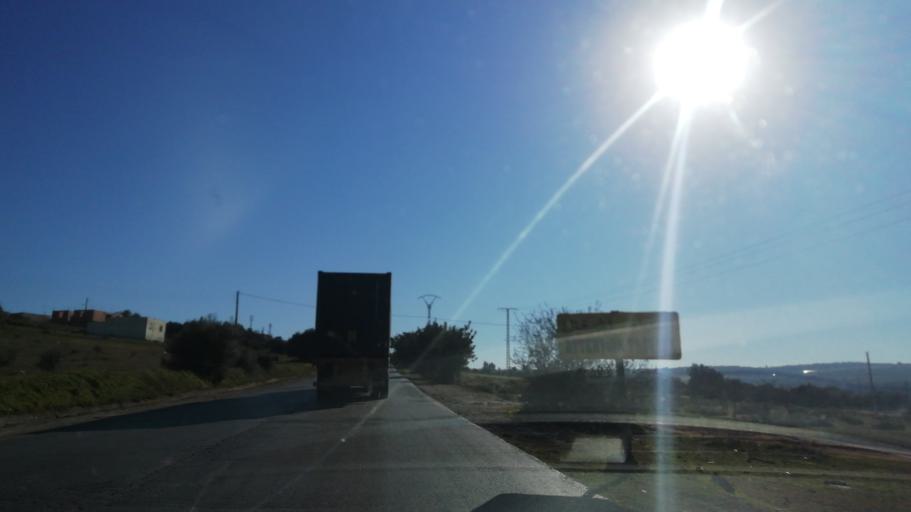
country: DZ
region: Relizane
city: Smala
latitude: 35.6793
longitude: 0.8001
